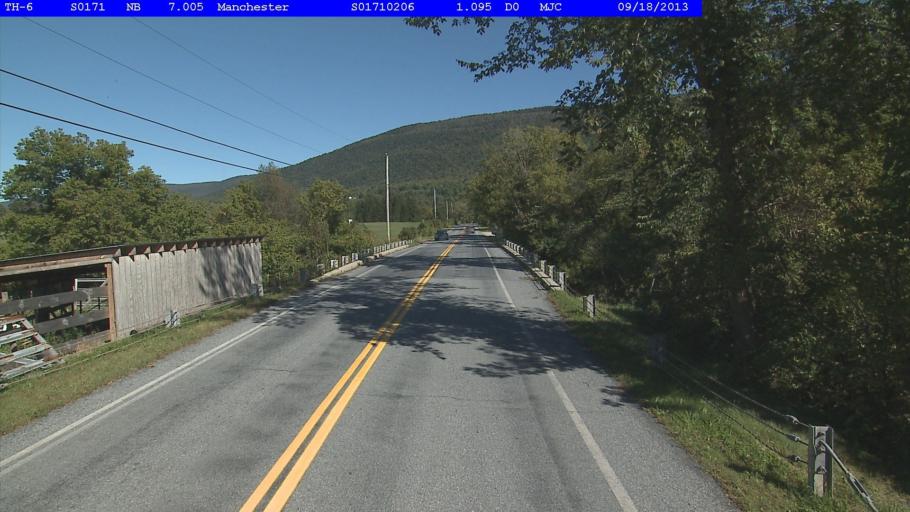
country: US
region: Vermont
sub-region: Bennington County
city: Manchester Center
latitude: 43.1323
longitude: -73.0805
